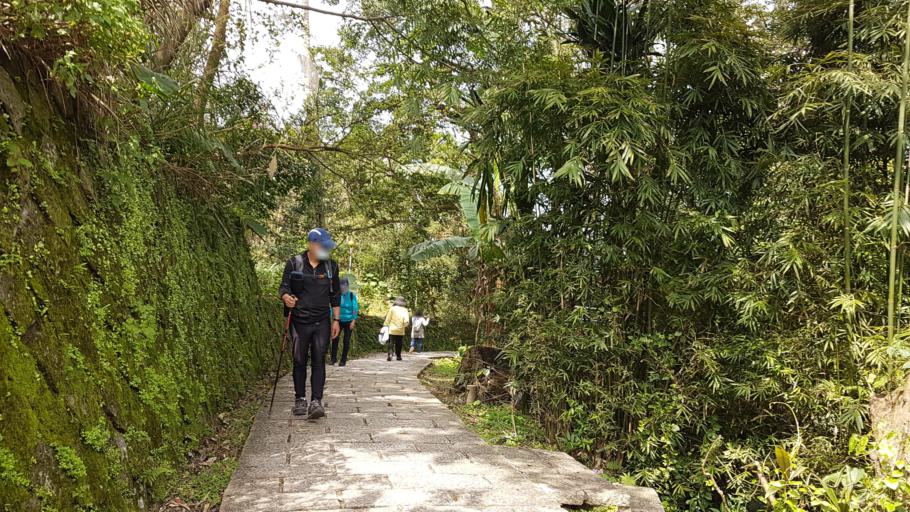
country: TW
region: Taipei
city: Taipei
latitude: 24.9692
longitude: 121.5811
